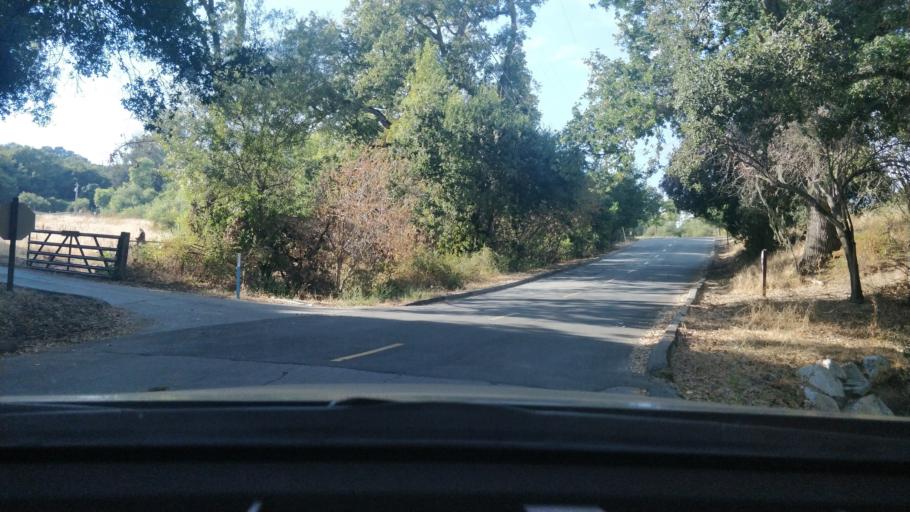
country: US
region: California
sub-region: Santa Clara County
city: East Foothills
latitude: 37.3390
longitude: -121.7197
